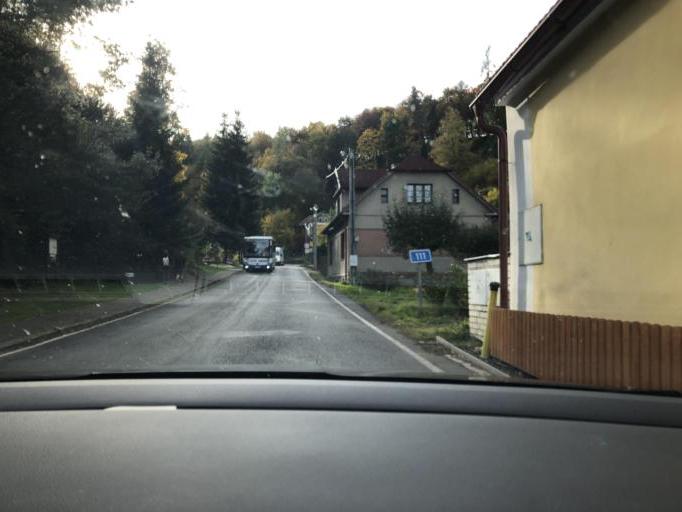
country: CZ
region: Central Bohemia
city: Divisov
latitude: 49.8105
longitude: 14.9273
